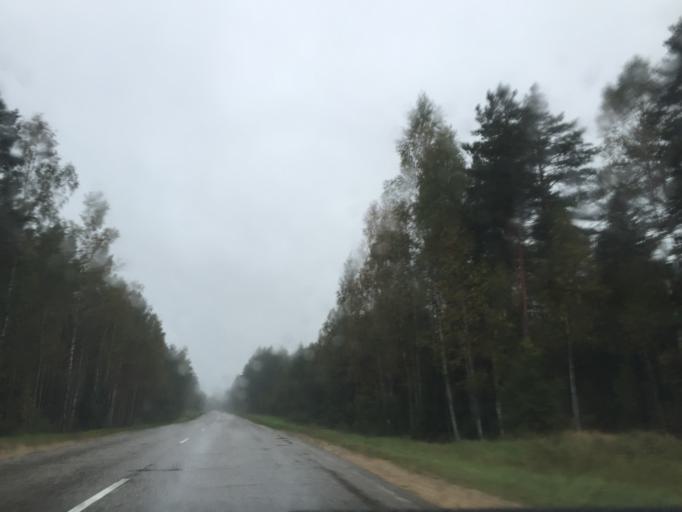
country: LV
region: Ropazu
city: Ropazi
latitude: 57.0067
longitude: 24.6755
